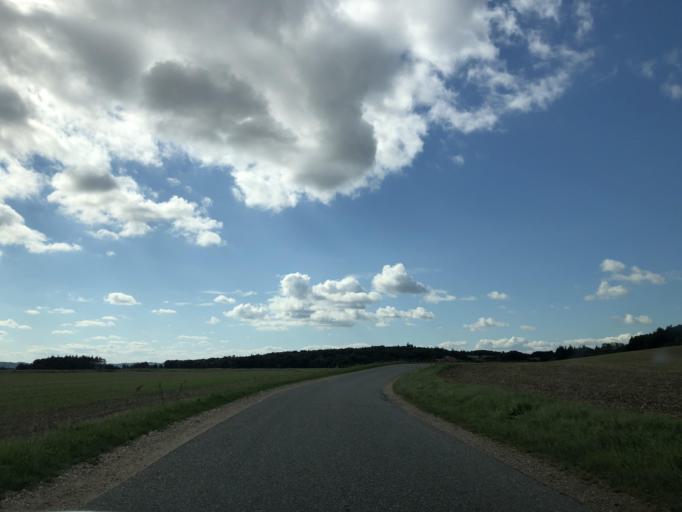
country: DK
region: Central Jutland
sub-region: Viborg Kommune
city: Viborg
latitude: 56.5711
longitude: 9.3388
